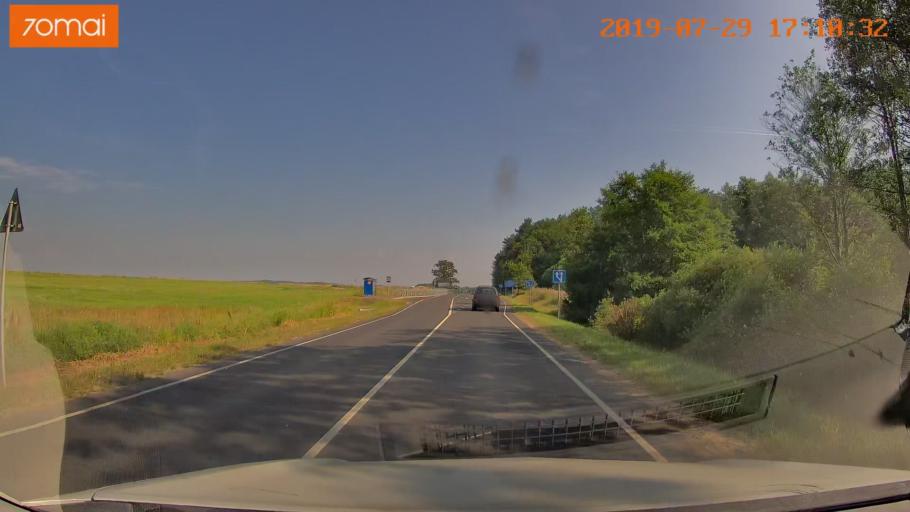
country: RU
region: Kaliningrad
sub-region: Gorod Kaliningrad
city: Kaliningrad
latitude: 54.8014
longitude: 20.3698
